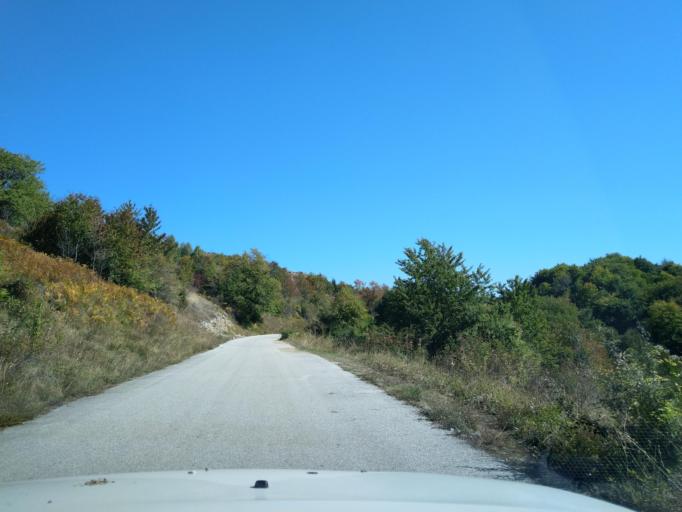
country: RS
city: Sokolovica
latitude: 43.2493
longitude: 20.3248
